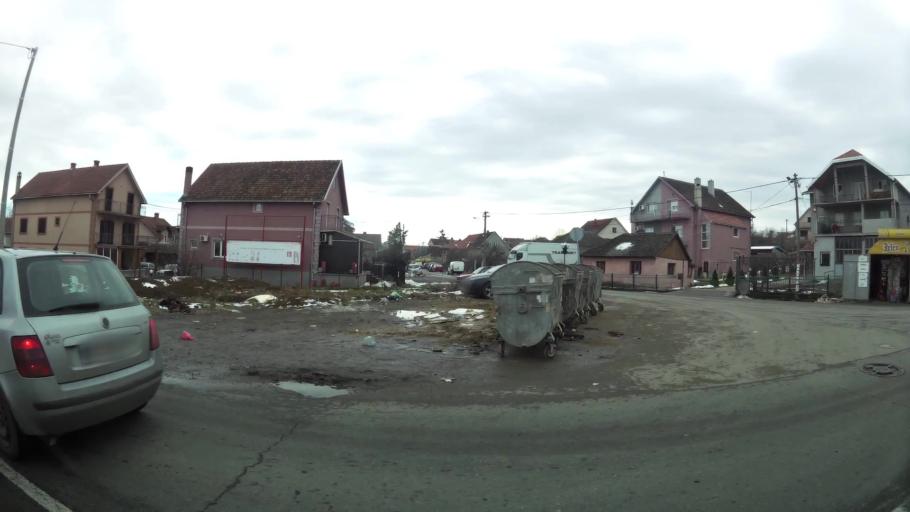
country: RS
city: Ostruznica
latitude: 44.7226
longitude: 20.3684
